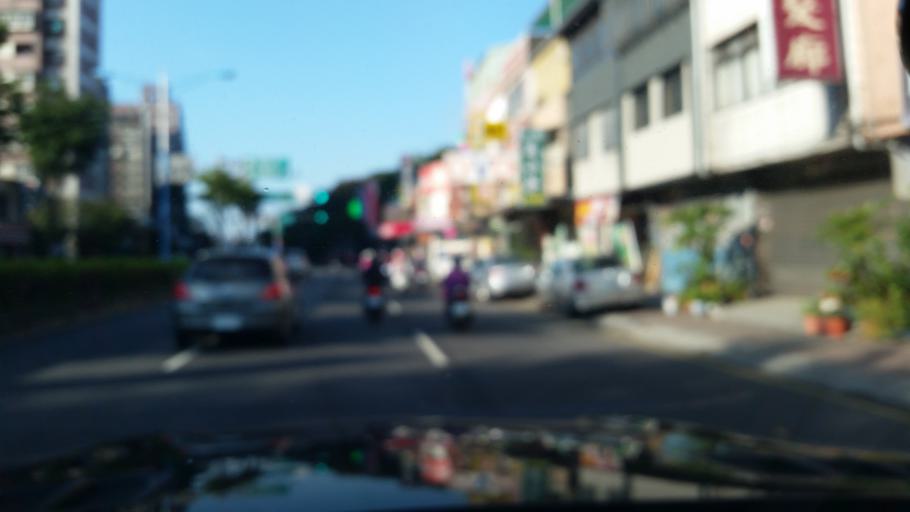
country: TW
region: Taiwan
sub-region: Taoyuan
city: Taoyuan
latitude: 25.0015
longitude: 121.3423
